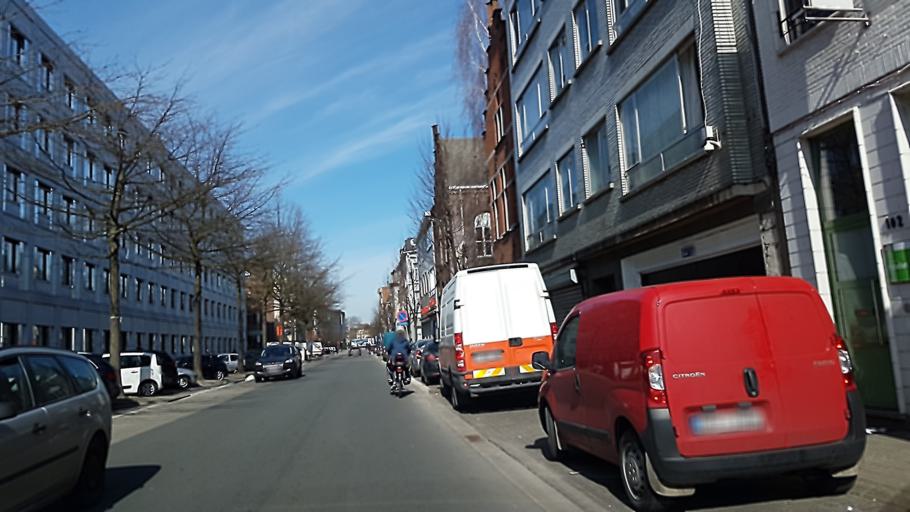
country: BE
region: Flanders
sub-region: Provincie Antwerpen
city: Antwerpen
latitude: 51.2235
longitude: 4.4368
